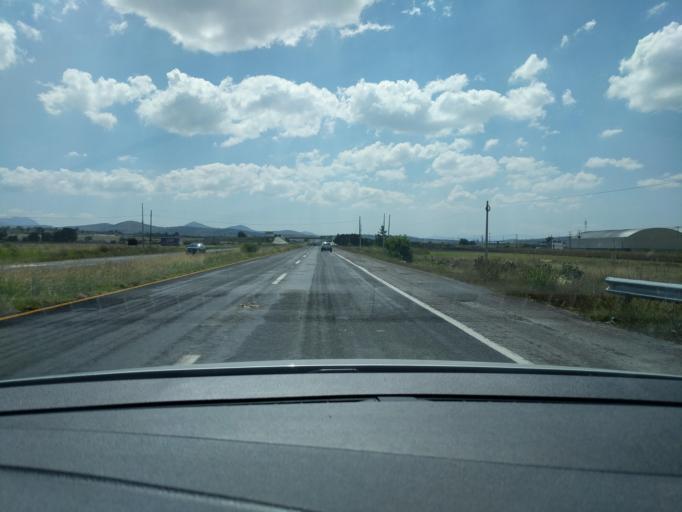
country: MX
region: Hidalgo
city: Zempoala
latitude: 19.9627
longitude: -98.6958
